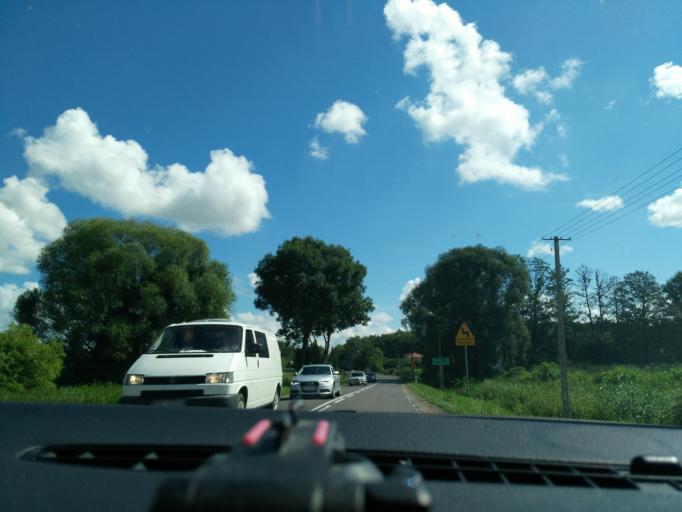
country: PL
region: Masovian Voivodeship
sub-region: Powiat losicki
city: Losice
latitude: 52.2436
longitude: 22.7782
